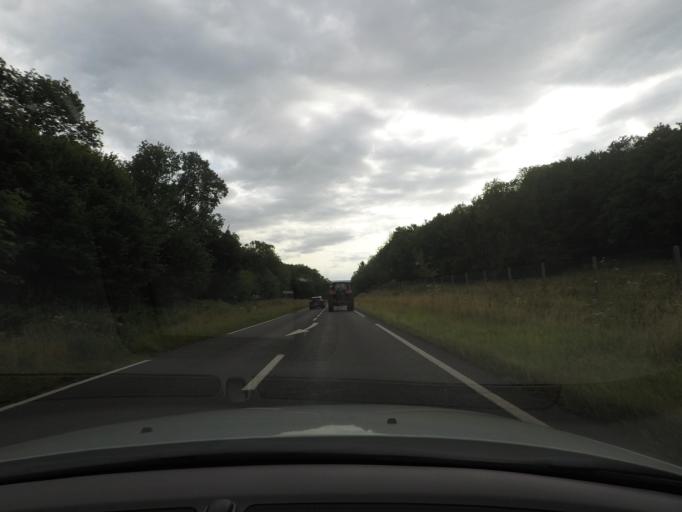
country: FR
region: Haute-Normandie
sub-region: Departement de la Seine-Maritime
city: Ymare
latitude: 49.3535
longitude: 1.1704
